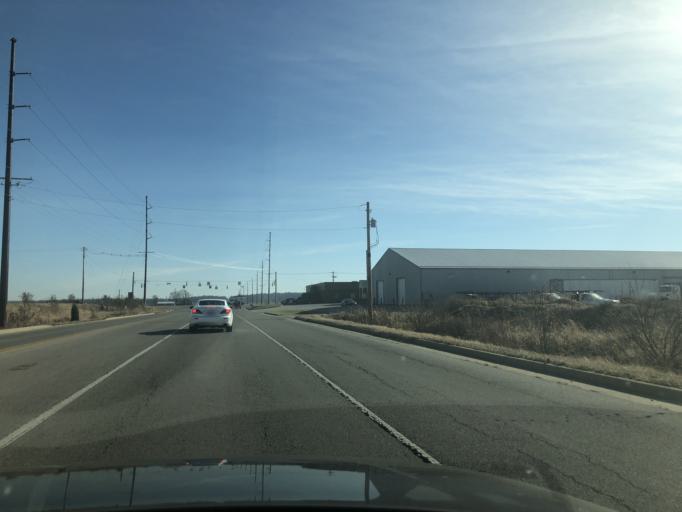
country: US
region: Indiana
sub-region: Warrick County
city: Newburgh
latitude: 37.9912
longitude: -87.4430
